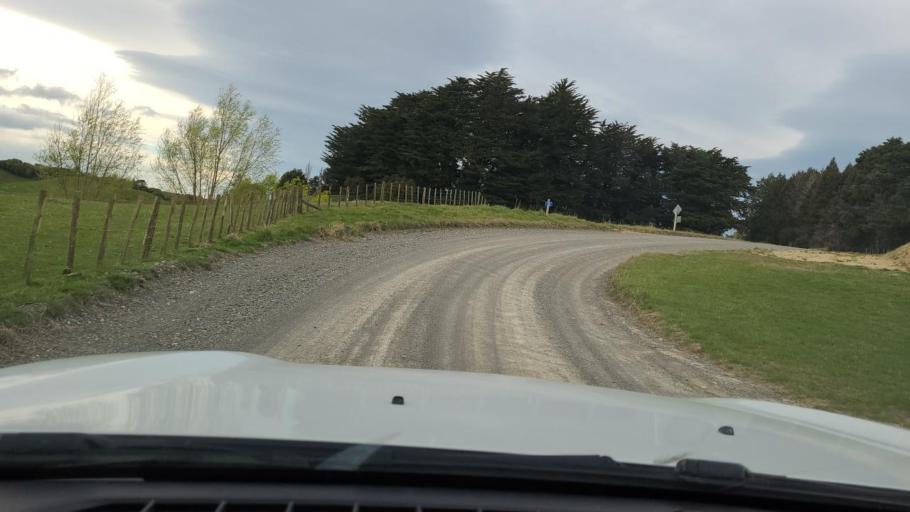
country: NZ
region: Hawke's Bay
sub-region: Napier City
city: Napier
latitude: -39.3220
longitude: 176.8346
